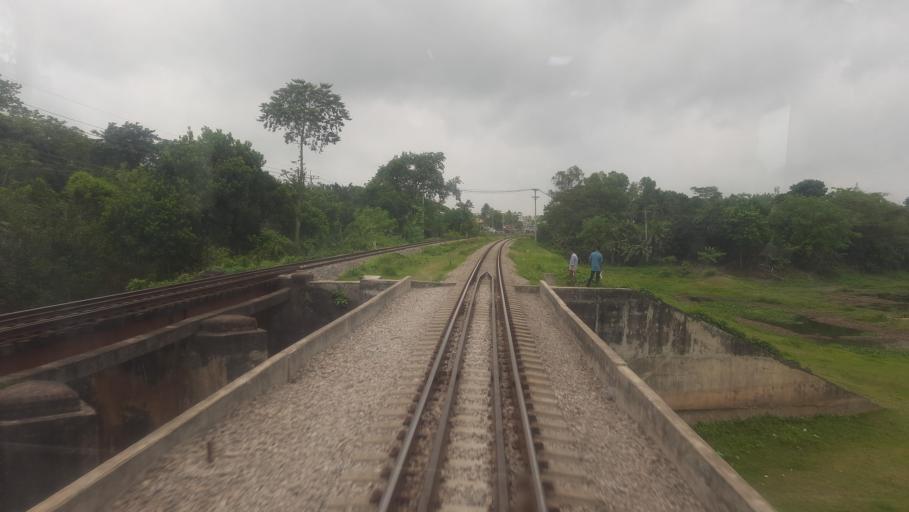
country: BD
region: Dhaka
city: Narsingdi
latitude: 23.9378
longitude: 90.7771
